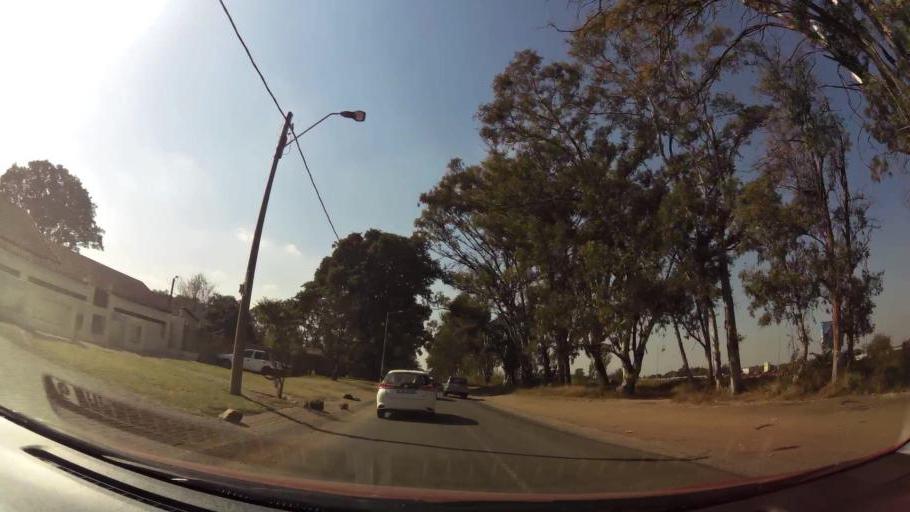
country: ZA
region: North-West
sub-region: Bojanala Platinum District Municipality
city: Rustenburg
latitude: -25.6616
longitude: 27.2337
